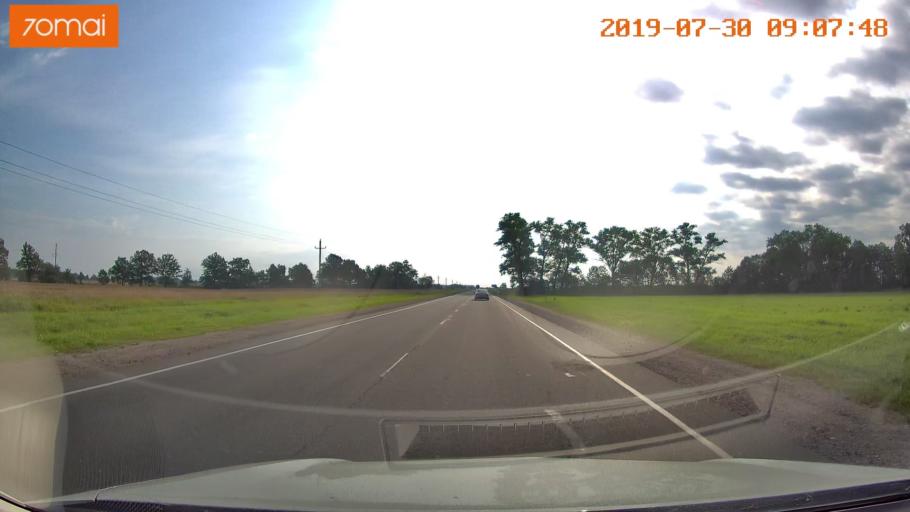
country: RU
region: Kaliningrad
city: Gusev
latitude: 54.6118
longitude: 22.3714
